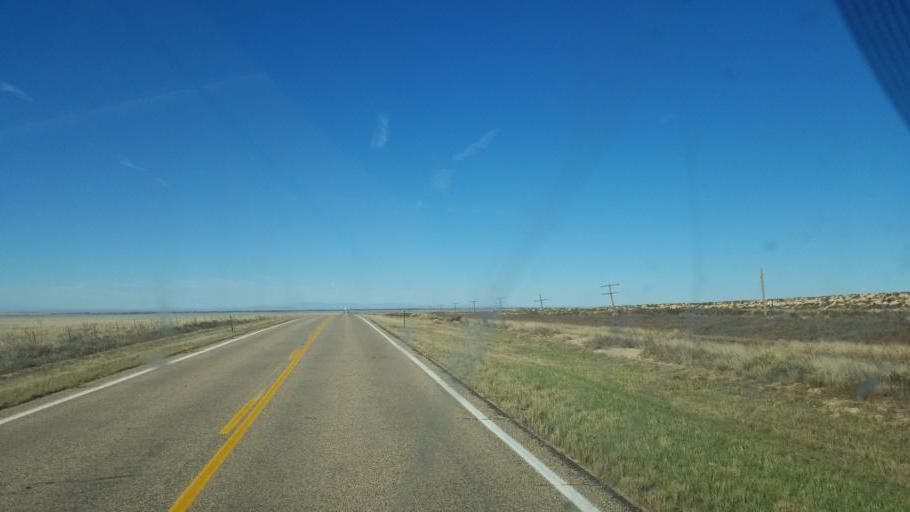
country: US
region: Colorado
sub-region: Crowley County
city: Ordway
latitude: 38.2613
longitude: -103.5254
